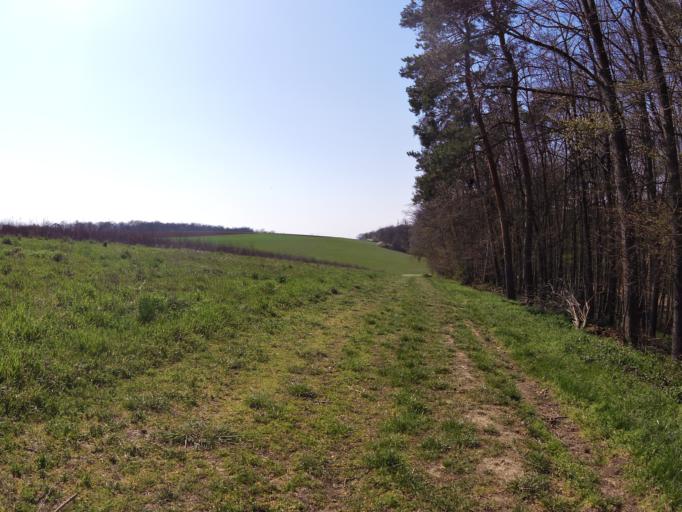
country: DE
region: Bavaria
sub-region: Regierungsbezirk Unterfranken
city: Rottendorf
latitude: 49.8217
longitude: 10.0722
